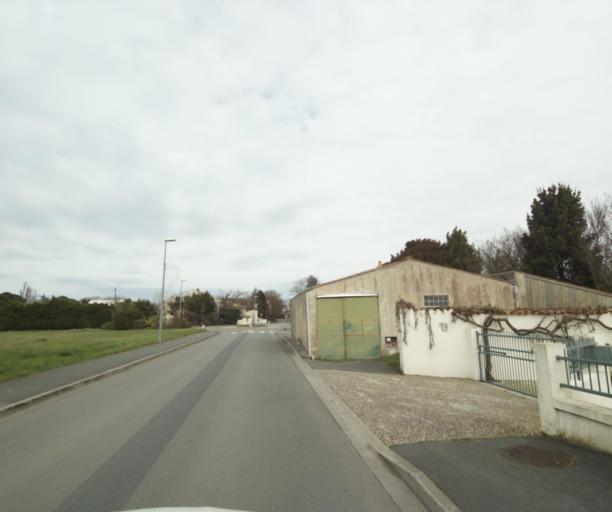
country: FR
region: Poitou-Charentes
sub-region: Departement de la Charente-Maritime
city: Lagord
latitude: 46.1853
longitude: -1.1663
